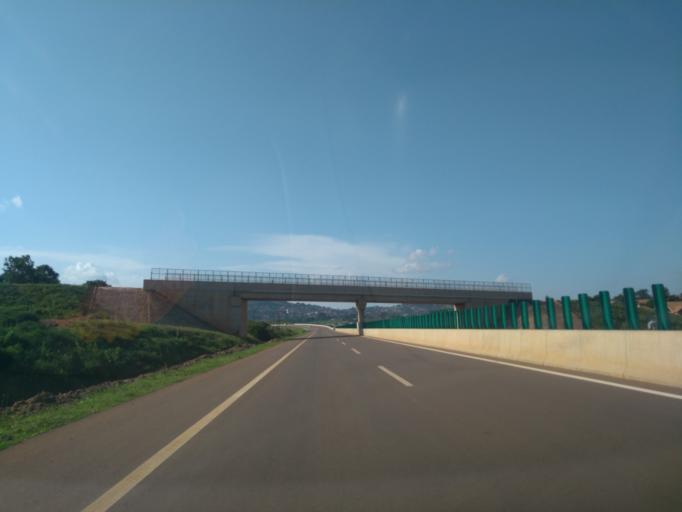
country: UG
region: Central Region
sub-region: Wakiso District
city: Kajansi
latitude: 0.2081
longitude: 32.5291
